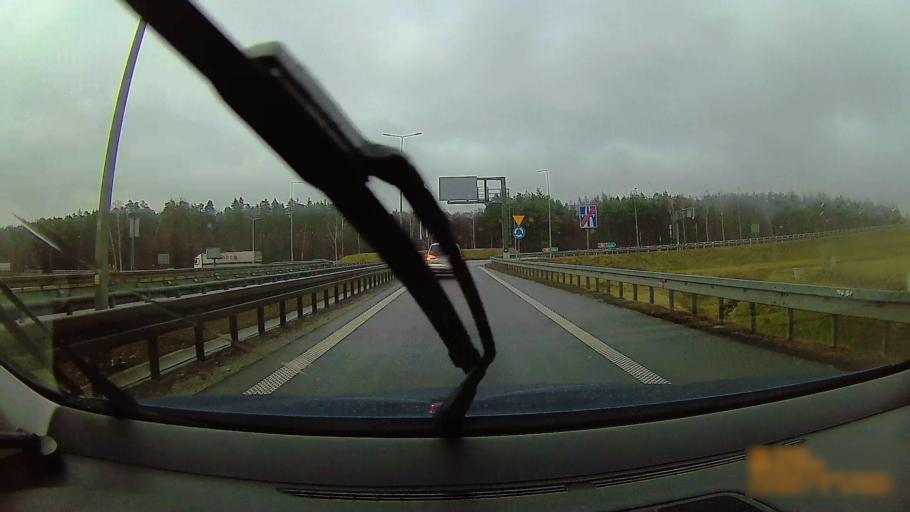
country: PL
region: Greater Poland Voivodeship
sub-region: Powiat koninski
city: Stare Miasto
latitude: 52.1566
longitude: 18.2721
